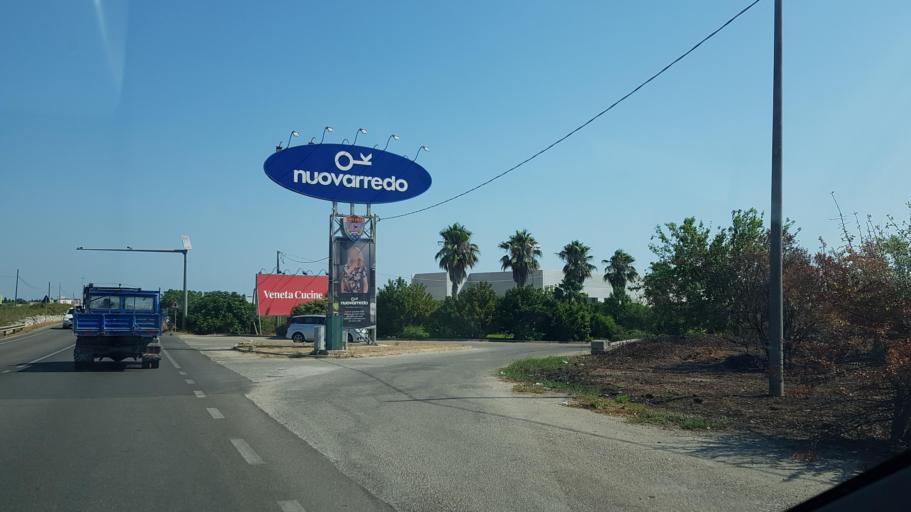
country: IT
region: Apulia
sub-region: Provincia di Lecce
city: Nociglia
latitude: 40.0139
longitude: 18.3243
